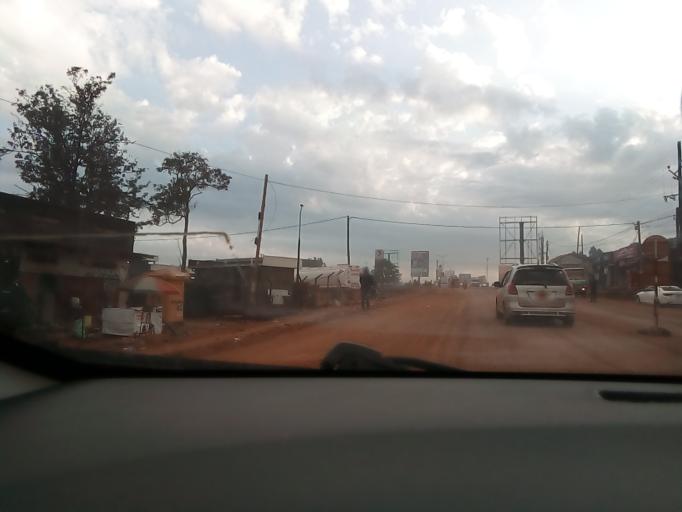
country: UG
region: Central Region
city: Masaka
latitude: -0.3098
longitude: 31.7634
